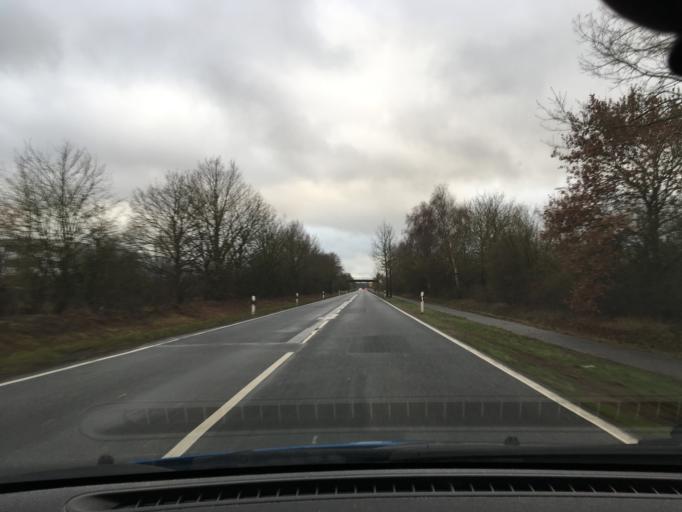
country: DE
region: Lower Saxony
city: Winsen
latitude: 53.3331
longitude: 10.2145
